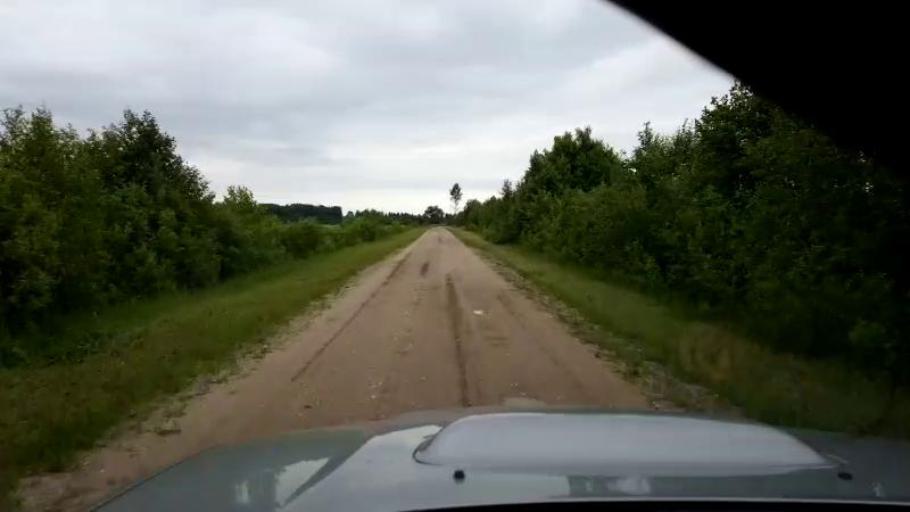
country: EE
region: Paernumaa
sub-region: Halinga vald
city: Parnu-Jaagupi
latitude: 58.5538
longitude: 24.5744
